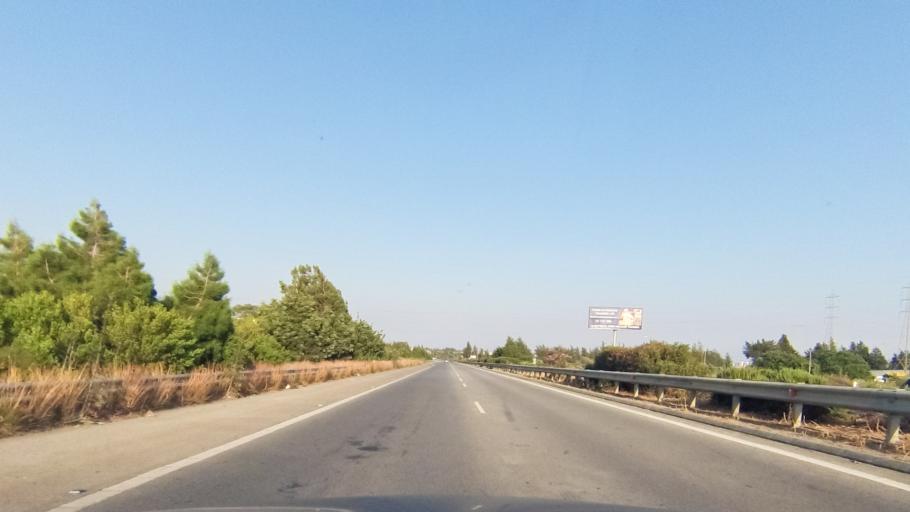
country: CY
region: Limassol
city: Ypsonas
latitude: 34.6906
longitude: 32.9799
